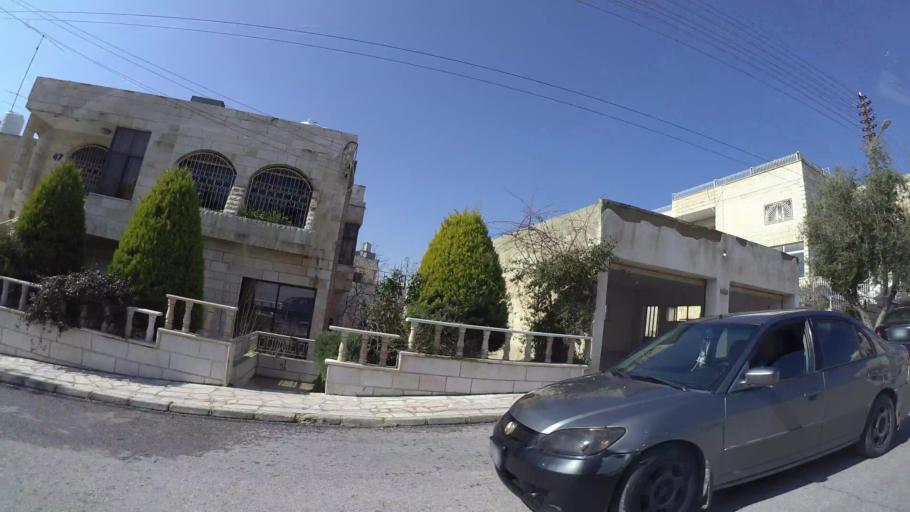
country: JO
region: Amman
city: Al Jubayhah
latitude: 31.9995
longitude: 35.8930
